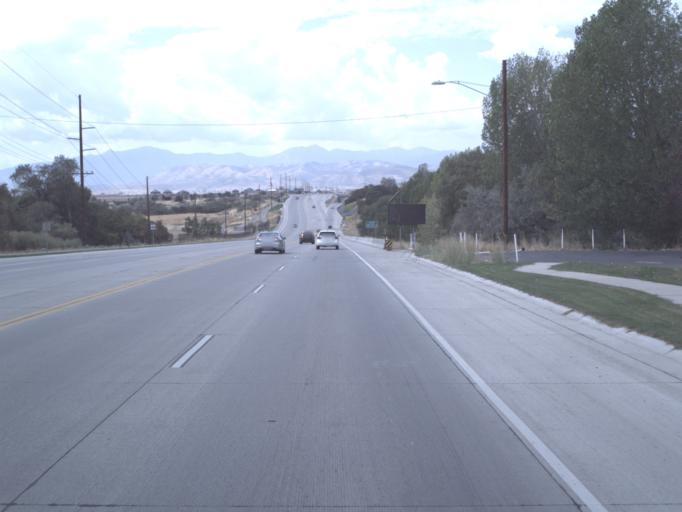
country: US
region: Utah
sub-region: Utah County
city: Alpine
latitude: 40.4319
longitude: -111.8119
